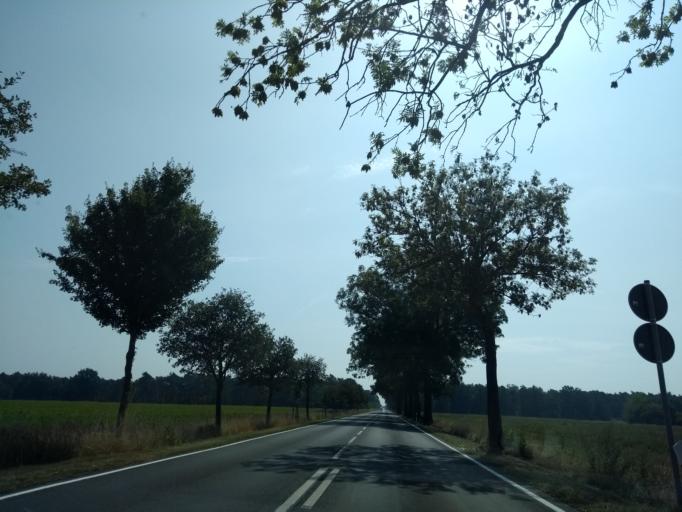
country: DE
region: Brandenburg
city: Lubbenau
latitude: 51.8307
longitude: 13.9967
